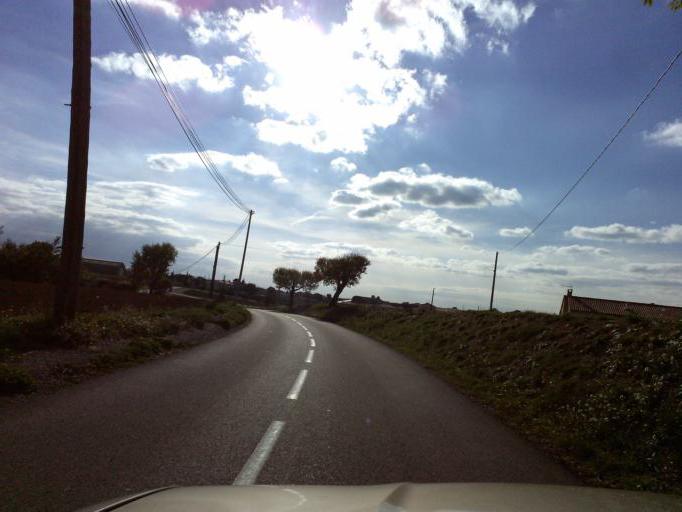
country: FR
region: Provence-Alpes-Cote d'Azur
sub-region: Departement des Alpes-de-Haute-Provence
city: Valensole
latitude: 43.8450
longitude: 5.9879
